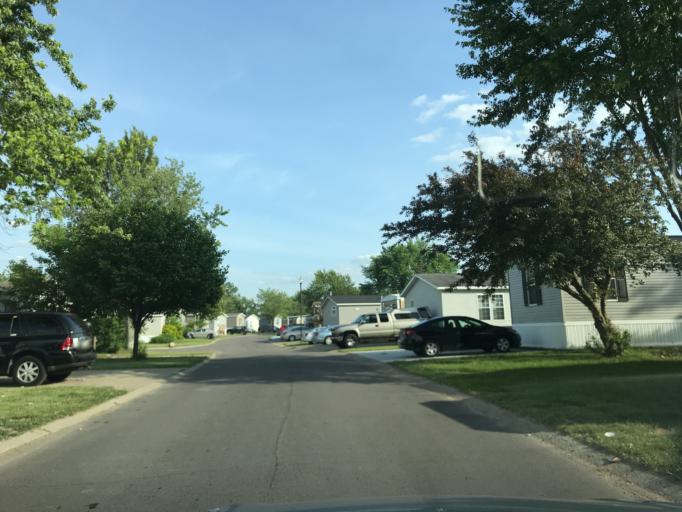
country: US
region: Michigan
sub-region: Oakland County
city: Walled Lake
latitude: 42.5144
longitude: -83.4601
